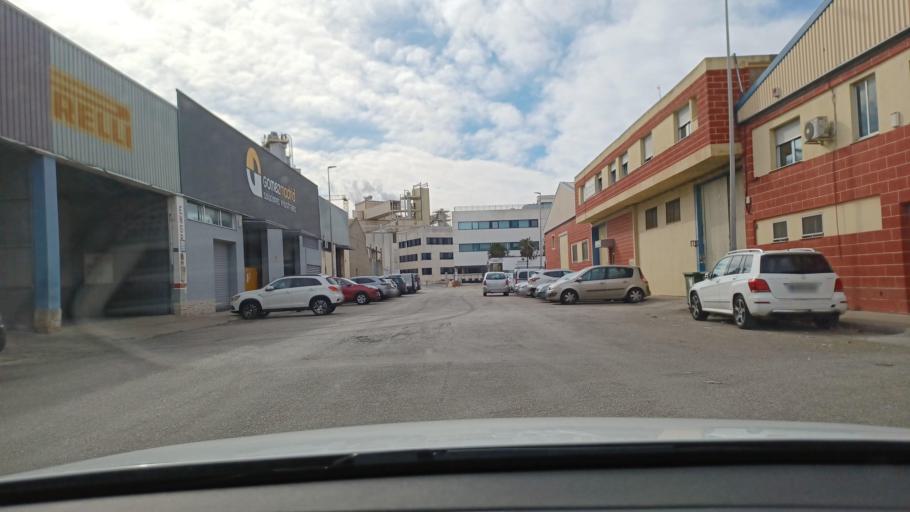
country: ES
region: Valencia
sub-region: Provincia de Valencia
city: Benifaio
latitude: 39.2853
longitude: -0.4320
